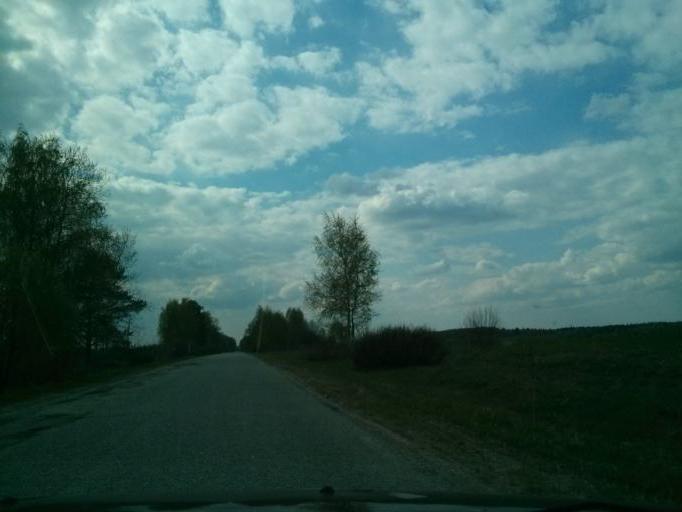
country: RU
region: Nizjnij Novgorod
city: Shimorskoye
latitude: 55.3379
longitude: 41.8902
